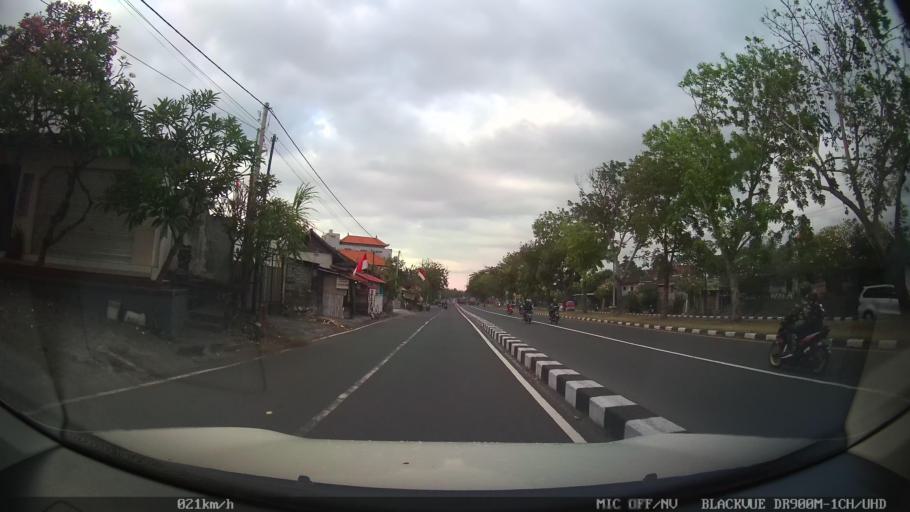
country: ID
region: Bali
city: Banjar Pasekan
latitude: -8.6428
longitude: 115.2786
